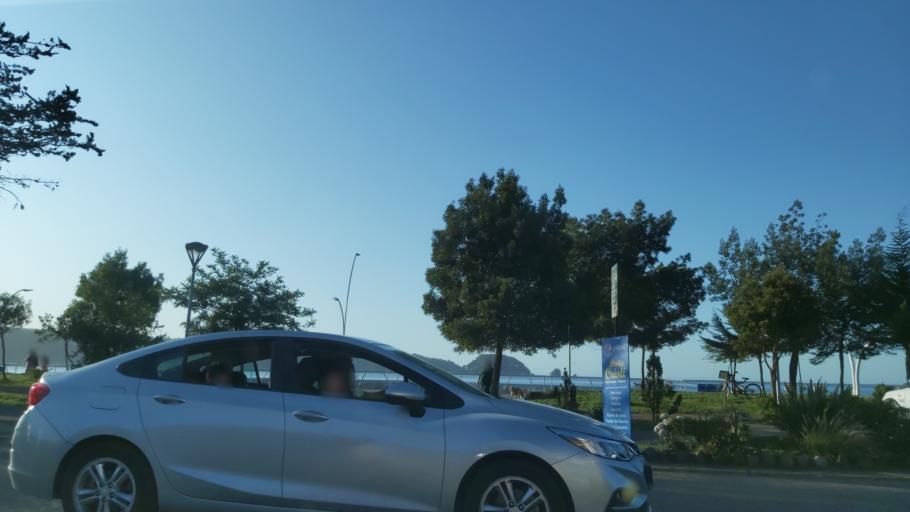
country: CL
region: Biobio
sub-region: Provincia de Concepcion
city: Tome
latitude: -36.5455
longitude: -72.9338
